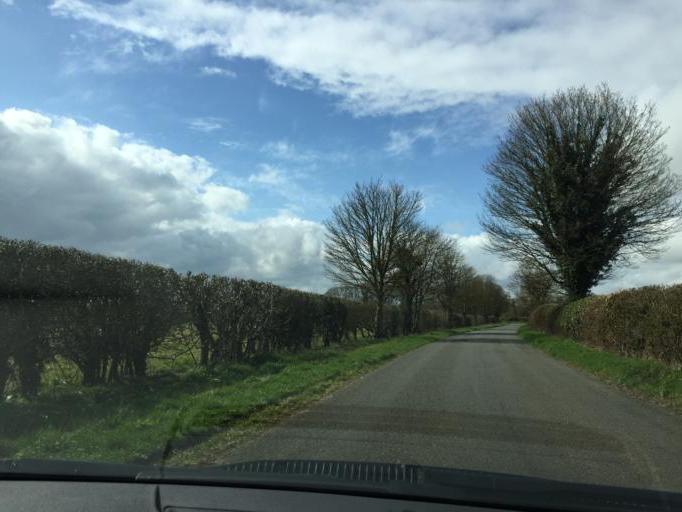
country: GB
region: England
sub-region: Oxfordshire
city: Woodstock
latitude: 51.8695
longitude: -1.3725
